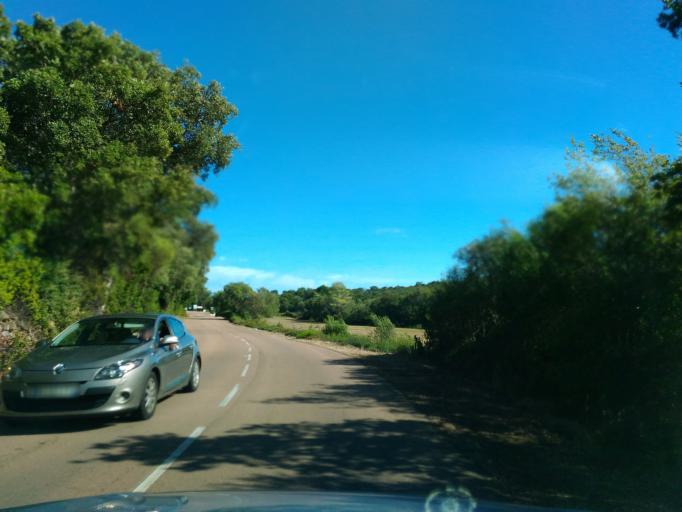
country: FR
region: Corsica
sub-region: Departement de la Corse-du-Sud
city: Porto-Vecchio
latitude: 41.6941
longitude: 9.3678
